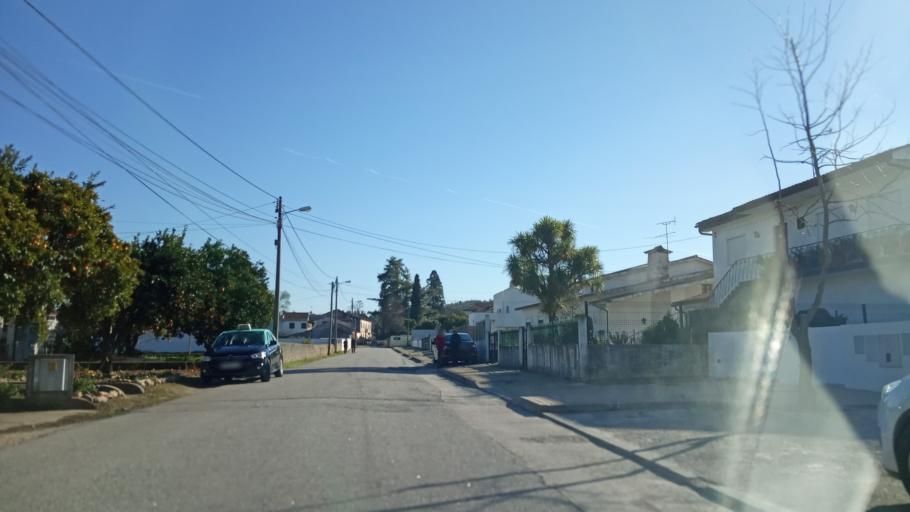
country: PT
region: Aveiro
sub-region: Anadia
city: Anadia
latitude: 40.4295
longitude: -8.4291
